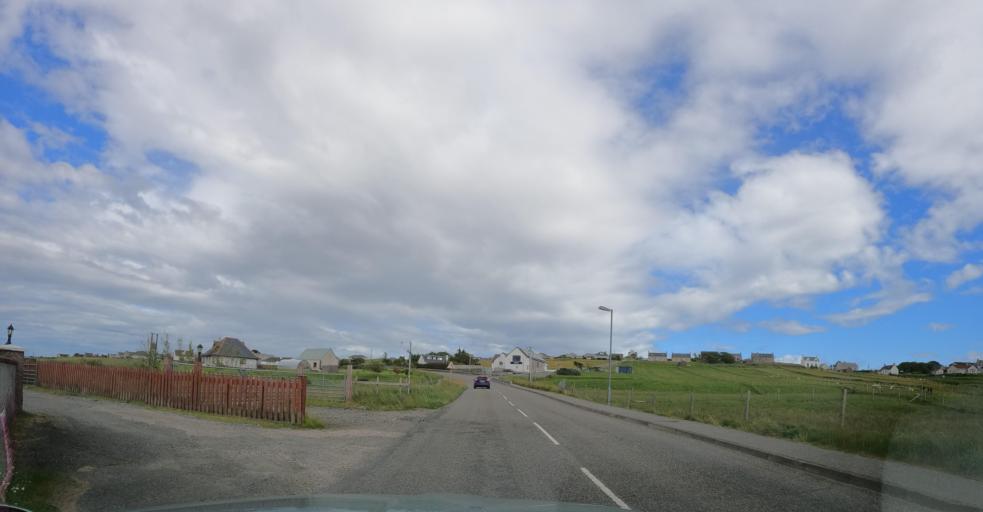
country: GB
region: Scotland
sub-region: Eilean Siar
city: Stornoway
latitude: 58.2048
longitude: -6.2725
